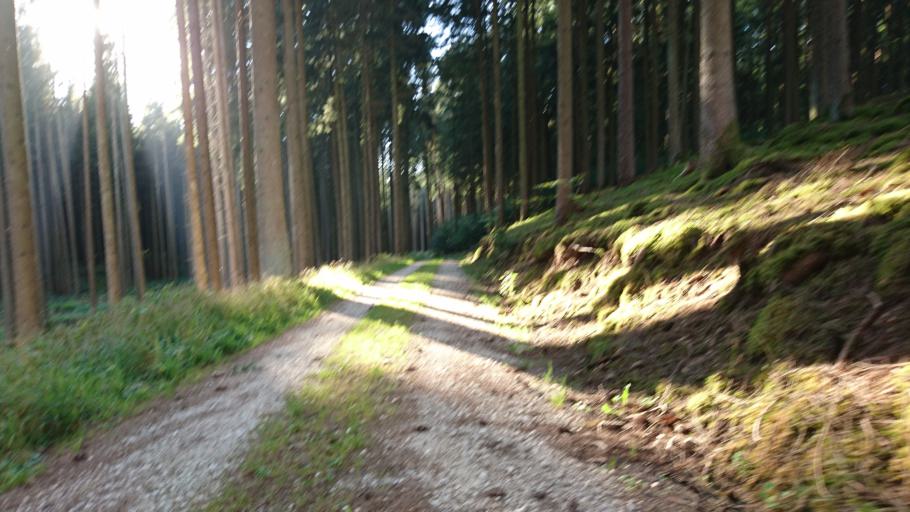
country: DE
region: Bavaria
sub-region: Swabia
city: Welden
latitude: 48.4326
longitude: 10.6275
